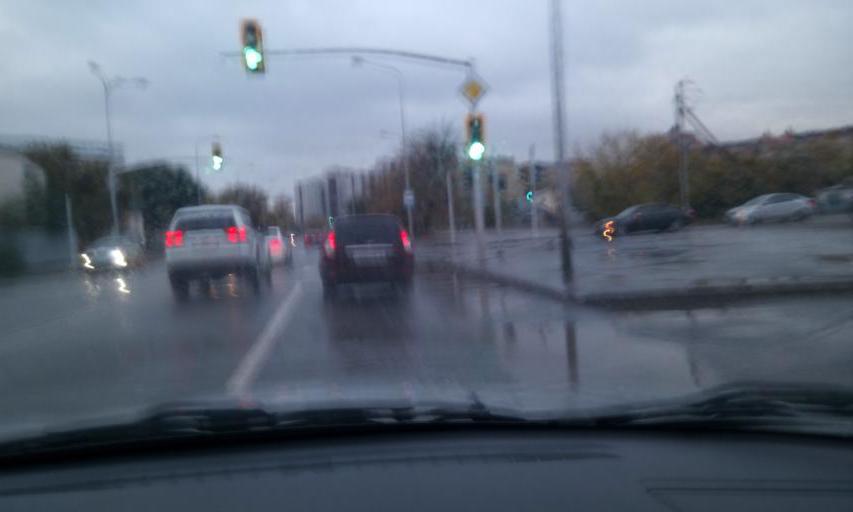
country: KZ
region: Astana Qalasy
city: Astana
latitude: 51.1637
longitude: 71.4504
